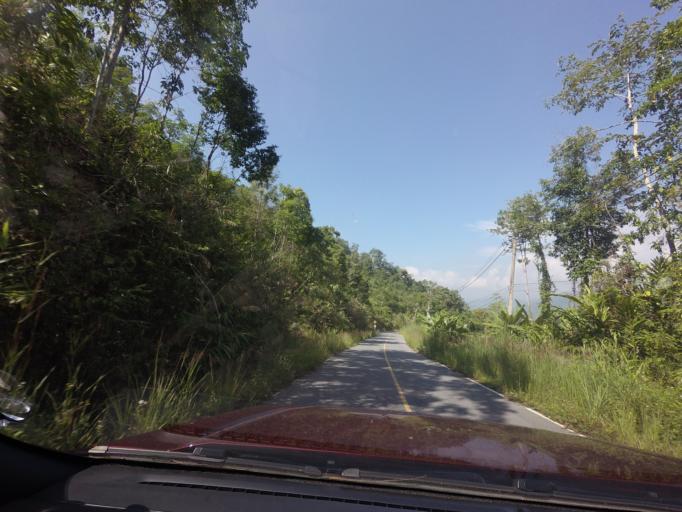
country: TH
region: Yala
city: Than To
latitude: 6.0065
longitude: 101.2203
